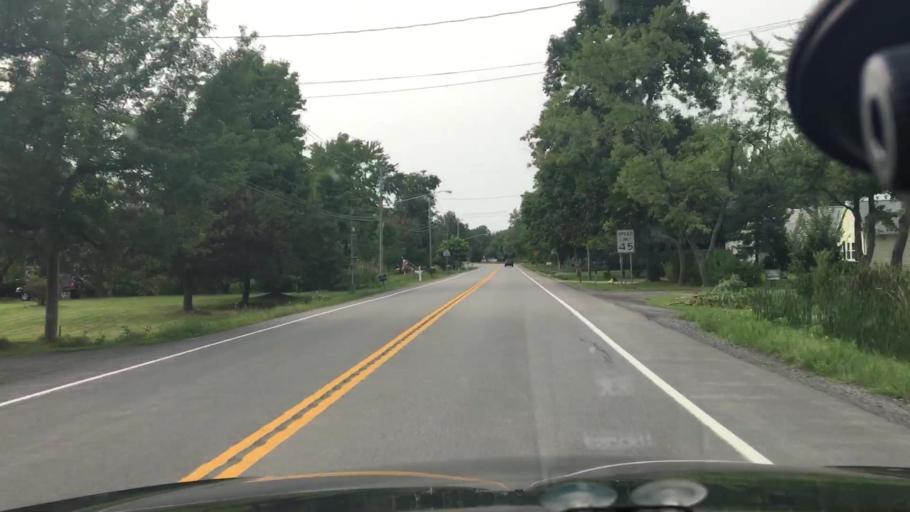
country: US
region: New York
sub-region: Erie County
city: Orchard Park
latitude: 42.7457
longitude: -78.7428
